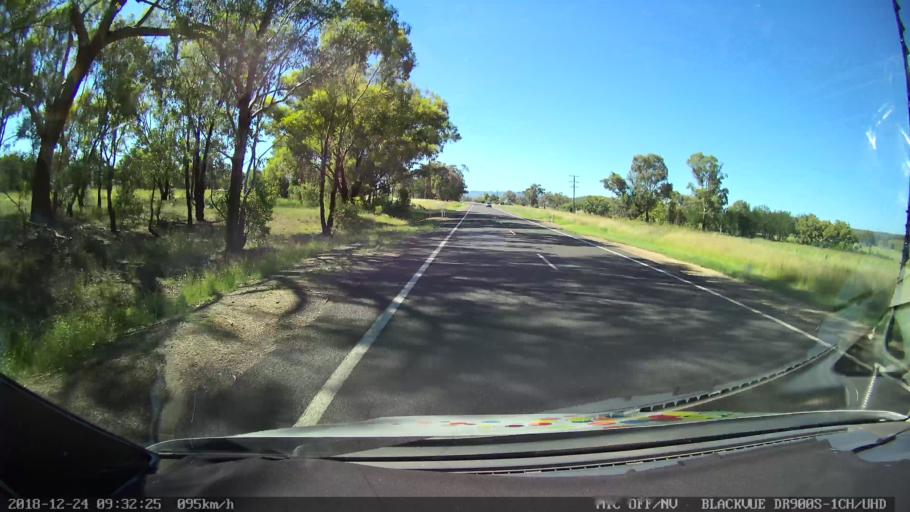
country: AU
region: New South Wales
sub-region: Liverpool Plains
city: Quirindi
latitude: -31.5899
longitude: 150.7023
